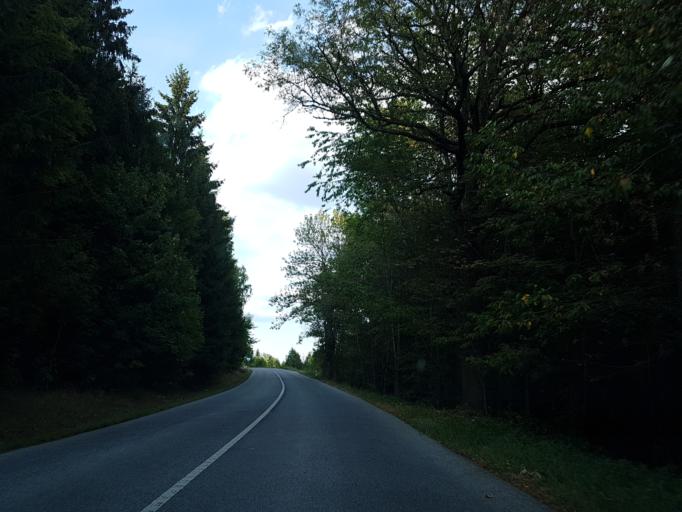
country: CZ
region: Liberecky
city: Mala Skala
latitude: 50.6596
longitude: 15.1667
